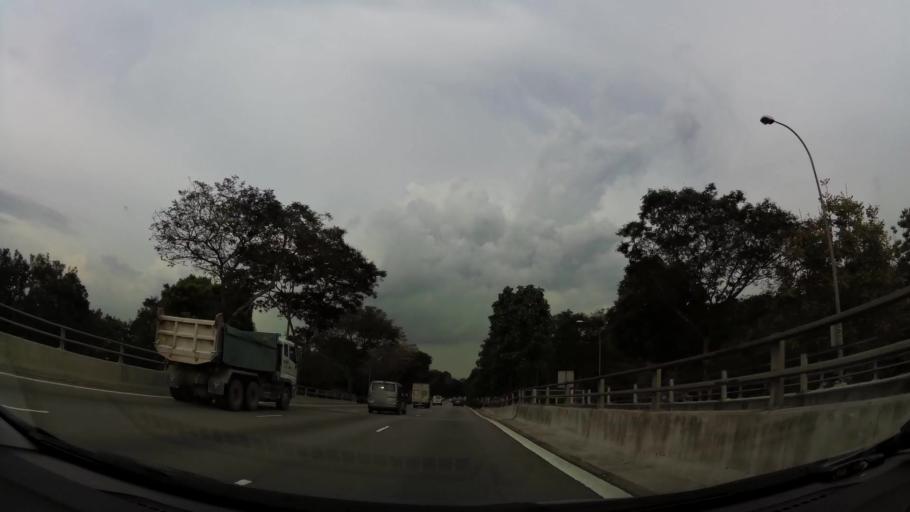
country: MY
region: Johor
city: Johor Bahru
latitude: 1.4225
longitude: 103.7725
